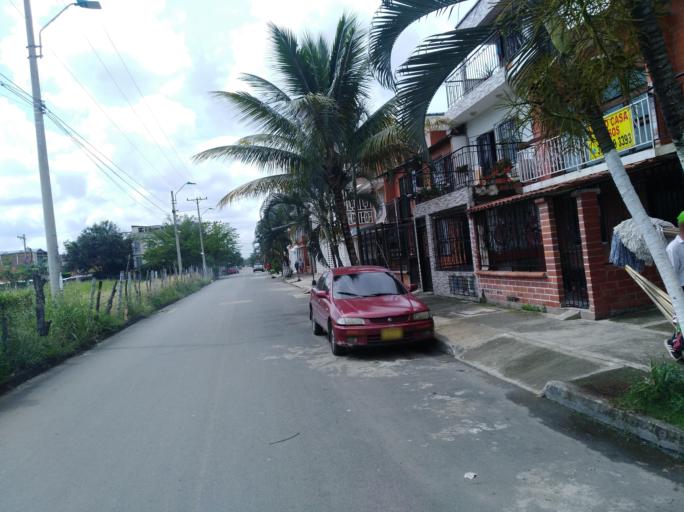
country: CO
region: Valle del Cauca
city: Cali
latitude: 3.3966
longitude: -76.5084
